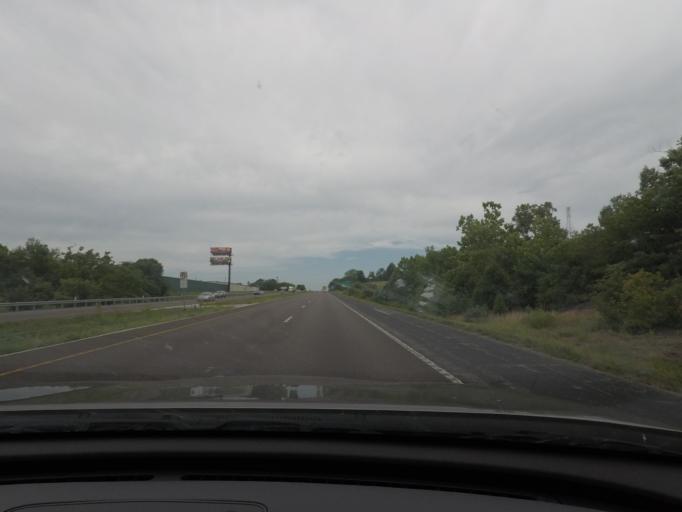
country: US
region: Missouri
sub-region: Boone County
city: Columbia
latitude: 38.9610
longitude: -92.2710
